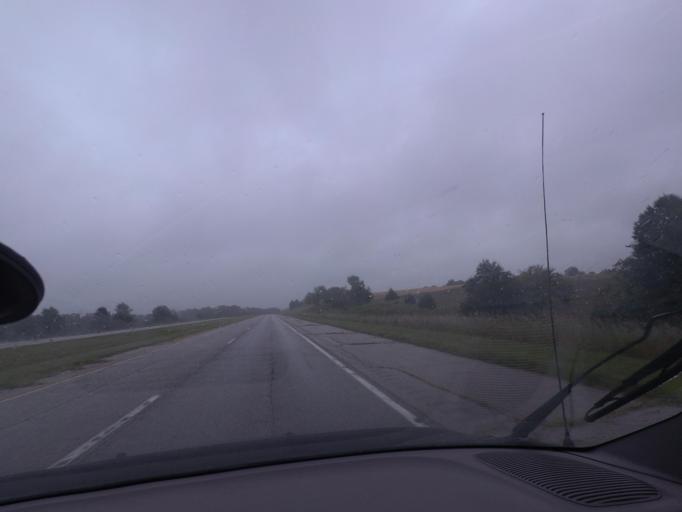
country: US
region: Illinois
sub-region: Pike County
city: Pittsfield
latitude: 39.6869
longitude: -90.8906
